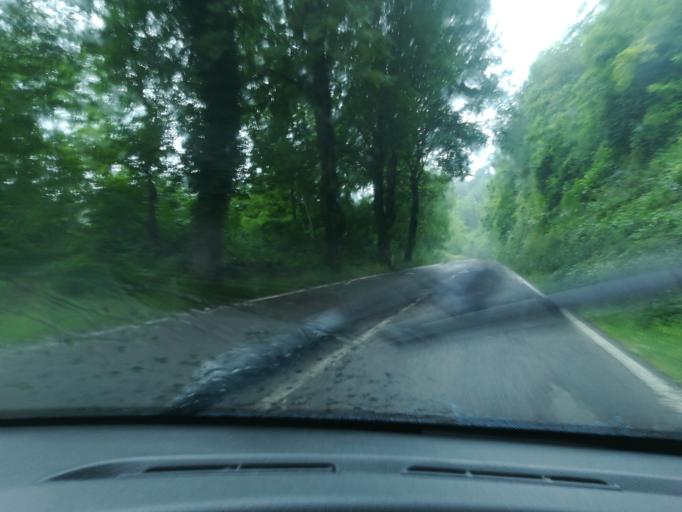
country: IT
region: The Marches
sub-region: Province of Fermo
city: Amandola
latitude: 43.0010
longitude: 13.3308
